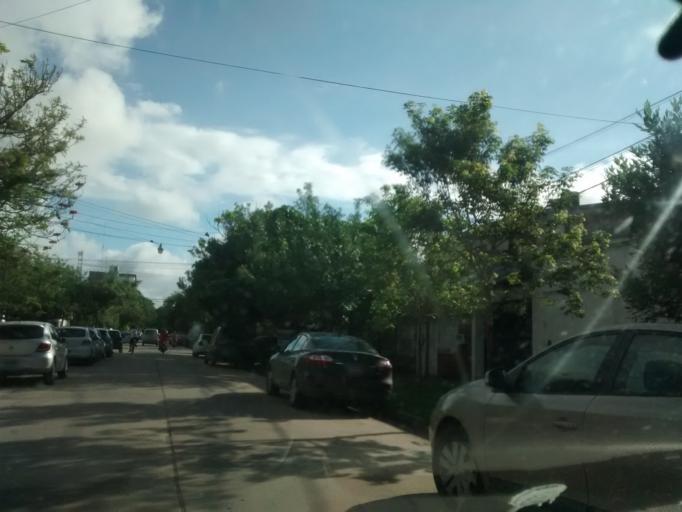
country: AR
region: Chaco
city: Resistencia
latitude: -27.4586
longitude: -58.9897
